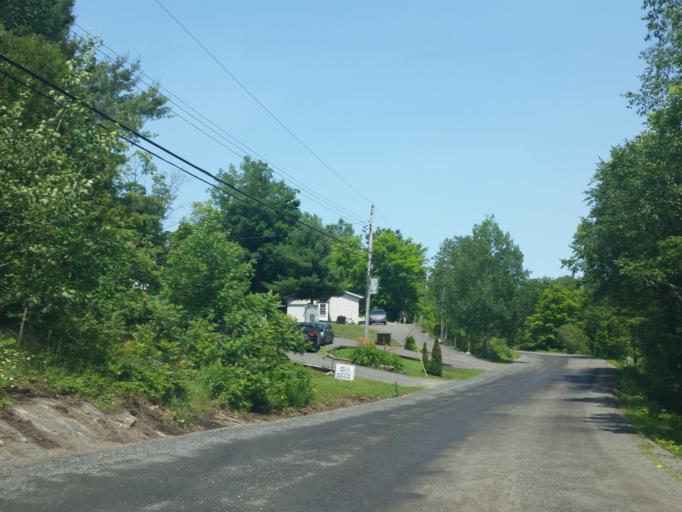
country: CA
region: Ontario
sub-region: Parry Sound District
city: Parry Sound
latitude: 45.4313
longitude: -80.0105
